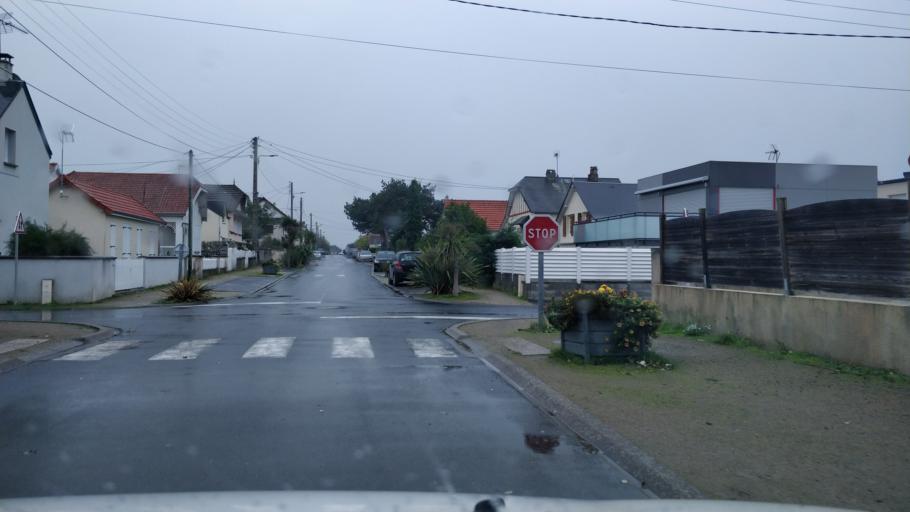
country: FR
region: Lower Normandy
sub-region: Departement de la Manche
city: Donville-les-Bains
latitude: 48.8974
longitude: -1.5674
